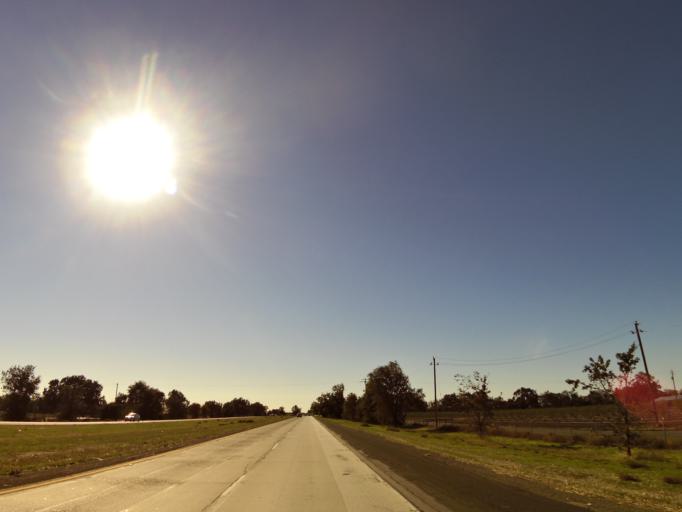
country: US
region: California
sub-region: Yolo County
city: Davis
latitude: 38.6065
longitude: -121.7671
